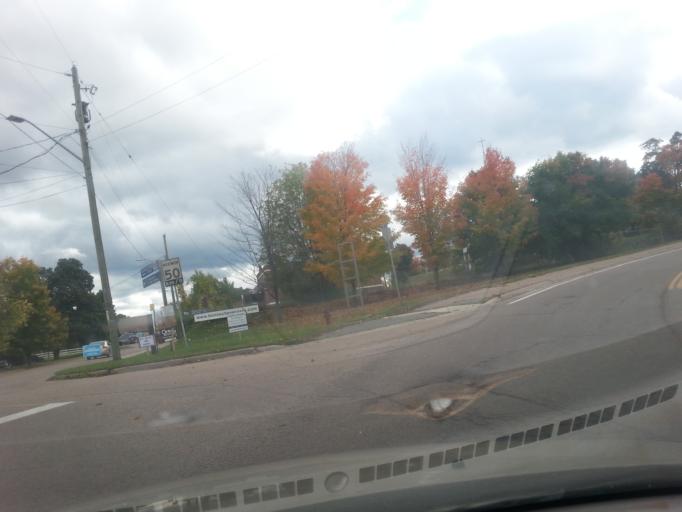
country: CA
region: Ontario
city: Pembroke
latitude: 45.5358
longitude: -77.0973
